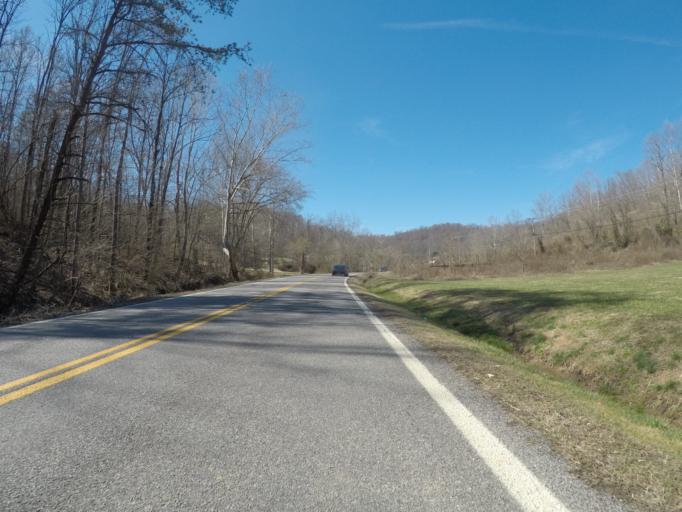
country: US
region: Ohio
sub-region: Lawrence County
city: Burlington
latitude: 38.4972
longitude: -82.5195
